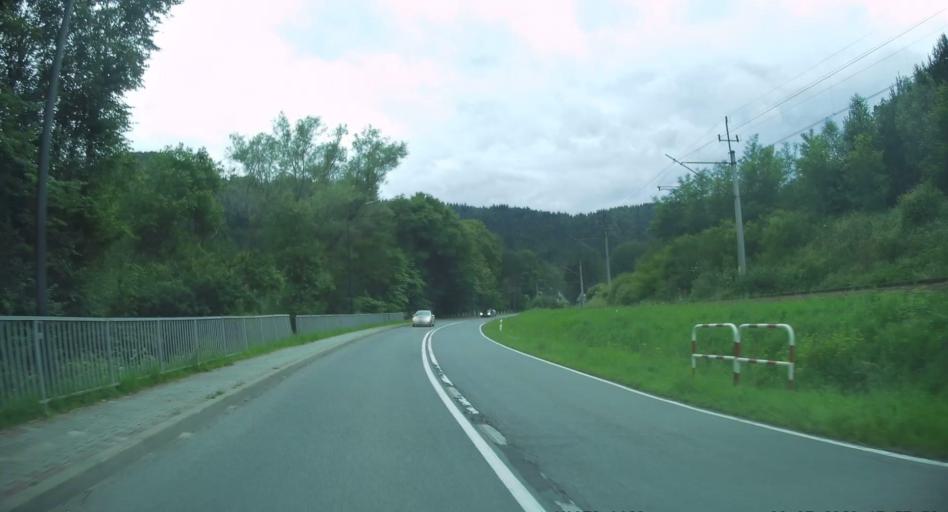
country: PL
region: Lesser Poland Voivodeship
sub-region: Powiat nowosadecki
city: Piwniczna-Zdroj
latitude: 49.3615
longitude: 20.7881
